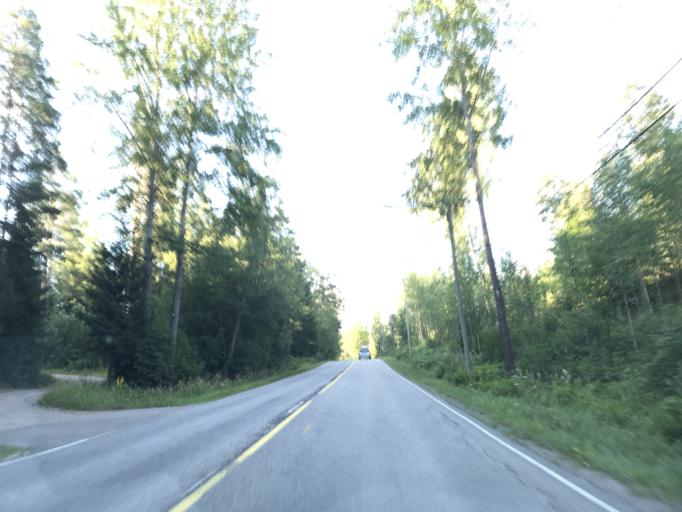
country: FI
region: Uusimaa
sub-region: Helsinki
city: Kauniainen
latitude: 60.3285
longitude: 24.7105
